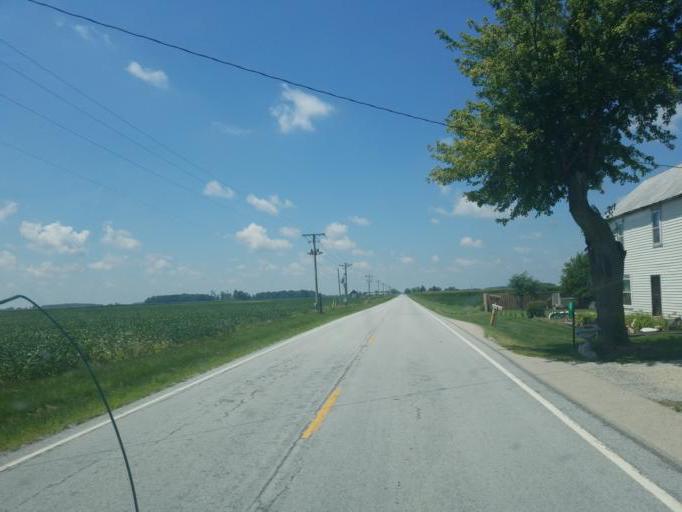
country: US
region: Ohio
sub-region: Allen County
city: Spencerville
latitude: 40.7141
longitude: -84.3901
